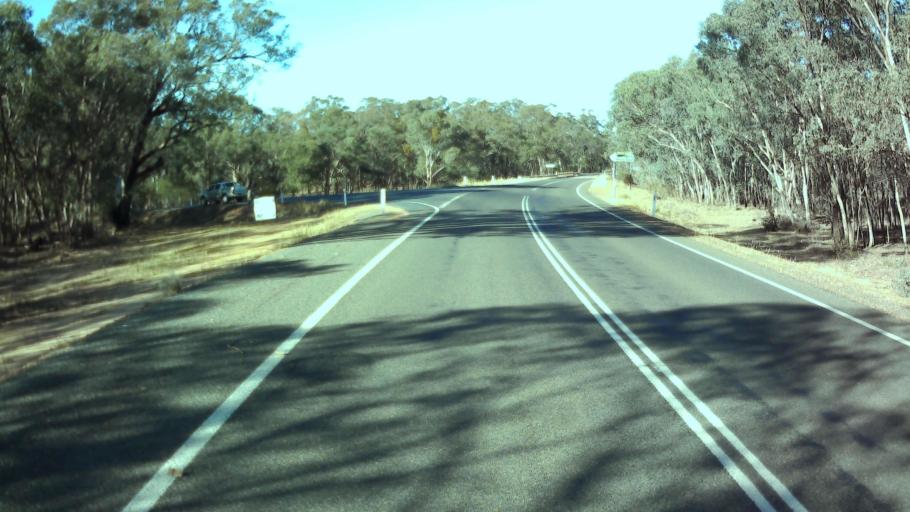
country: AU
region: New South Wales
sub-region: Weddin
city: Grenfell
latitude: -34.0001
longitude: 148.1310
